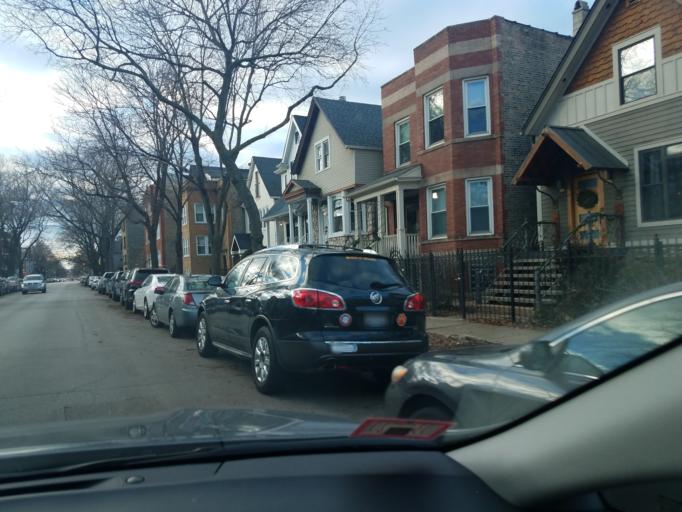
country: US
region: Illinois
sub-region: Cook County
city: Lincolnwood
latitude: 41.9433
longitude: -87.6763
